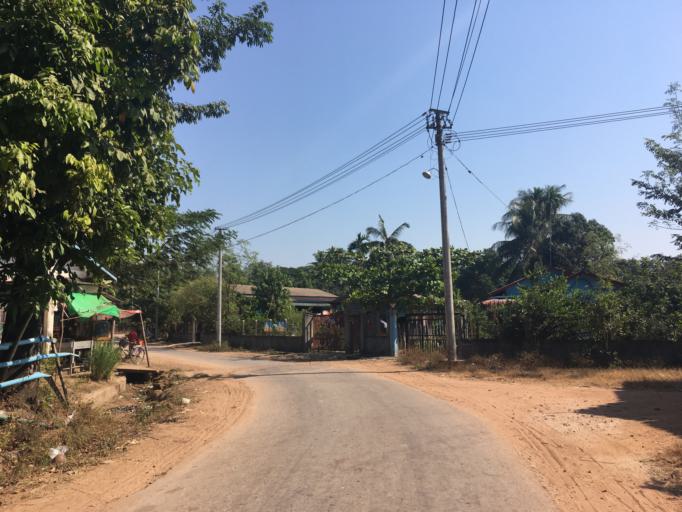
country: MM
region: Mon
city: Mawlamyine
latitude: 16.4317
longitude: 97.7047
